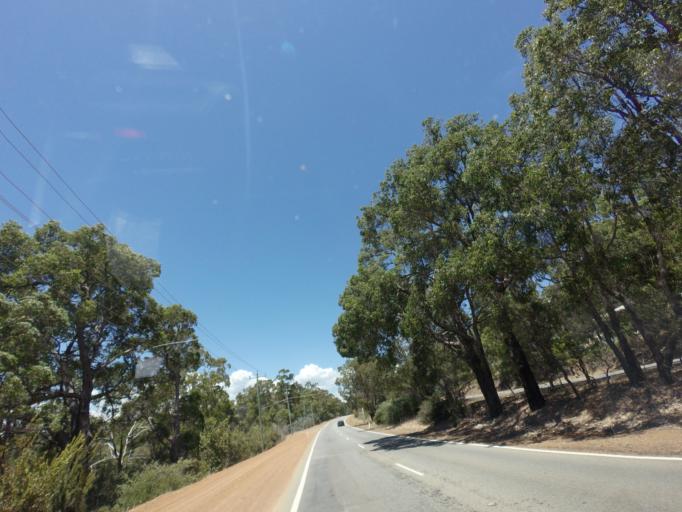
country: AU
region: Western Australia
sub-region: Mundaring
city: Parkerville
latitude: -31.8992
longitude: 116.1253
